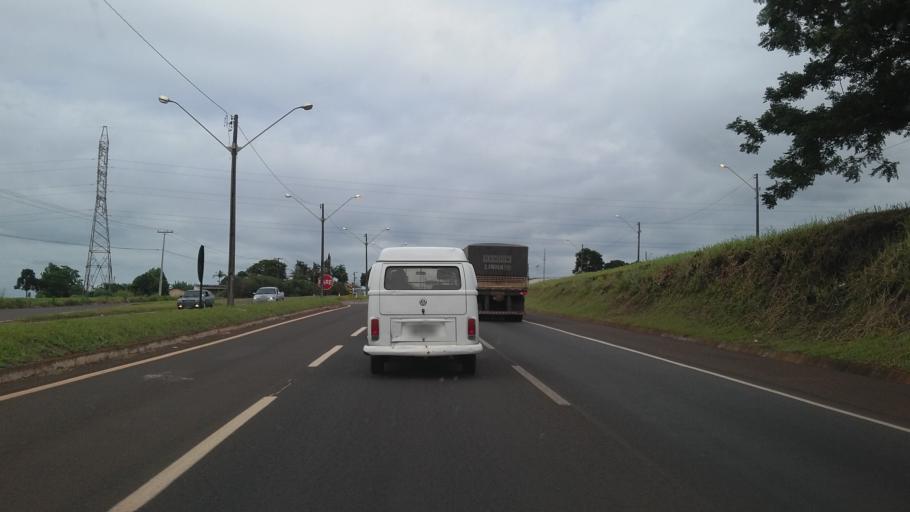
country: BR
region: Parana
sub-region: Londrina
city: Londrina
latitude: -23.2931
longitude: -51.1228
